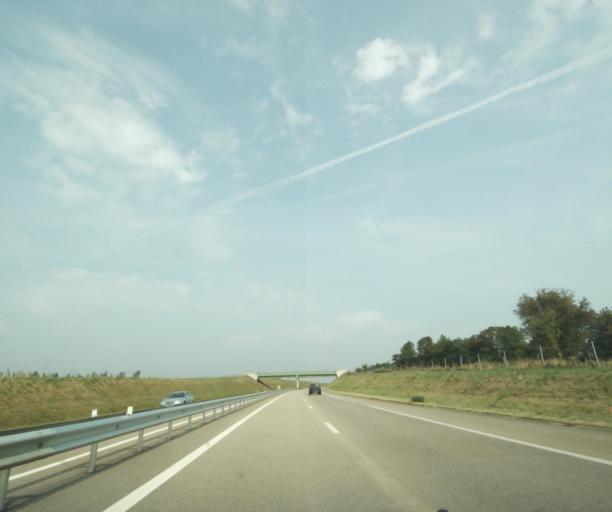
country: FR
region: Lower Normandy
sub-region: Departement du Calvados
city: Falaise
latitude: 48.8781
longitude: -0.2186
